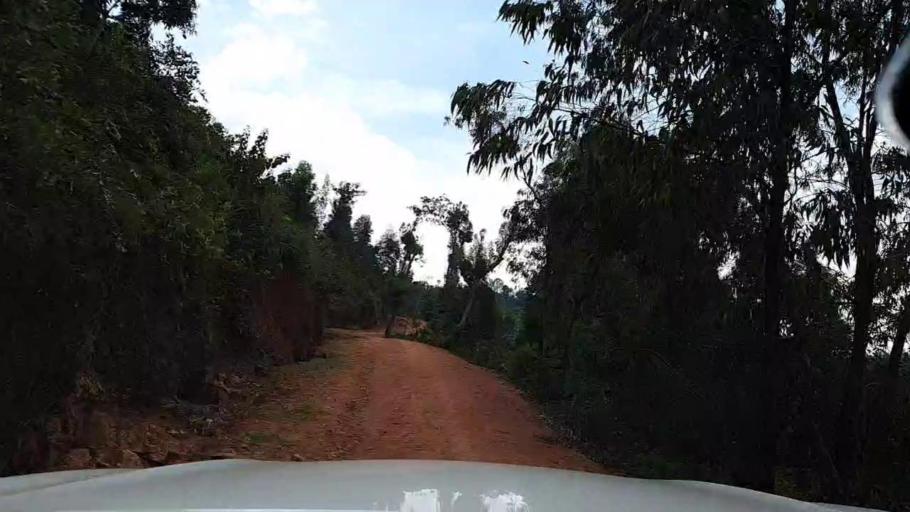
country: RW
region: Southern Province
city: Butare
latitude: -2.7470
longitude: 29.7629
